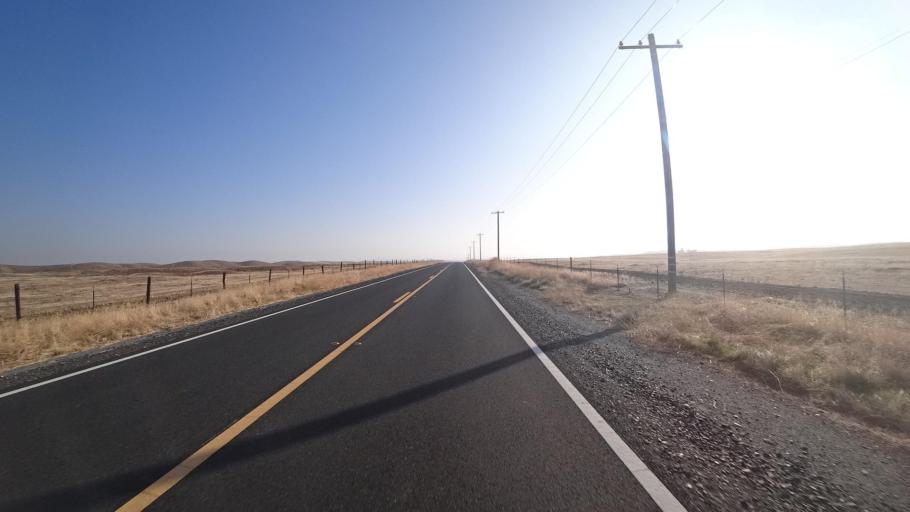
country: US
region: California
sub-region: Tulare County
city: Richgrove
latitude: 35.7620
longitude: -119.0429
